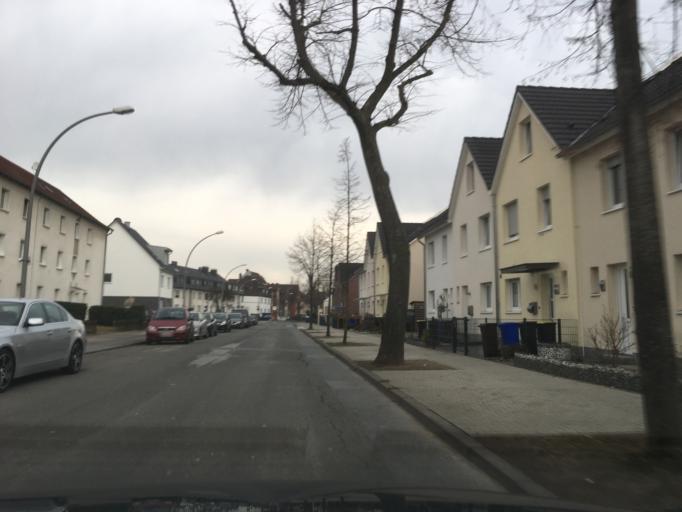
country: DE
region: North Rhine-Westphalia
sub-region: Regierungsbezirk Munster
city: Gladbeck
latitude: 51.5548
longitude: 7.0075
